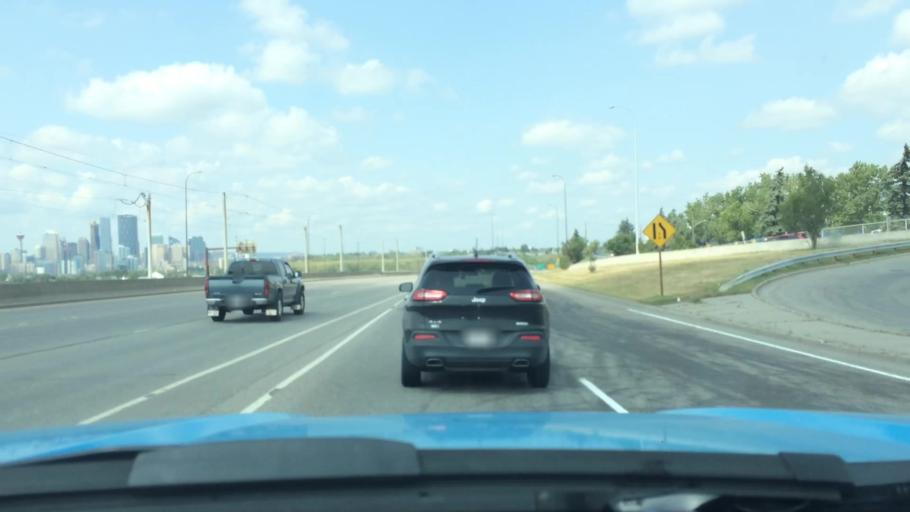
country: CA
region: Alberta
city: Calgary
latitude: 51.0463
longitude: -114.0077
